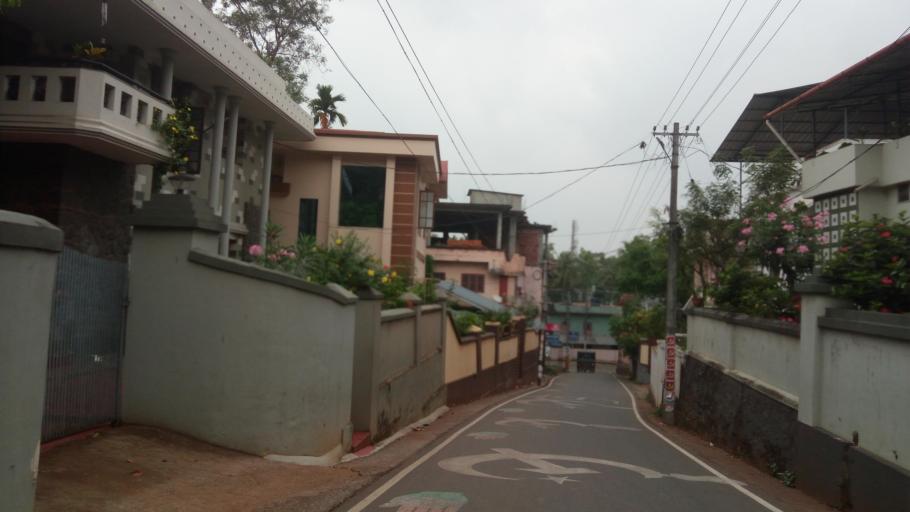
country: IN
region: Kerala
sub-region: Malappuram
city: Malappuram
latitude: 10.9931
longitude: 76.0088
